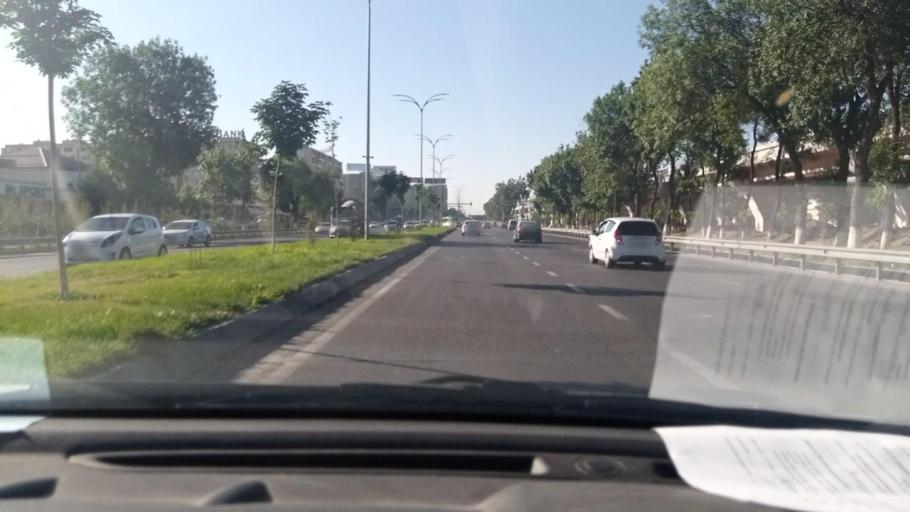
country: UZ
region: Toshkent
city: Salor
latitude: 41.2944
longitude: 69.3544
